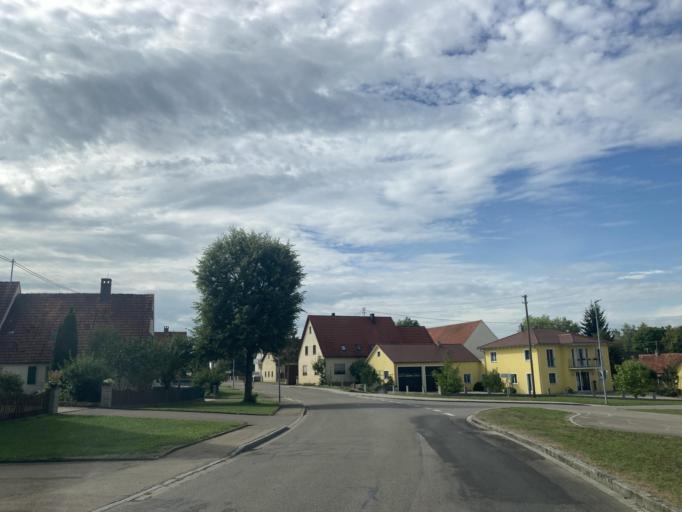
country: DE
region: Bavaria
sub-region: Swabia
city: Alerheim
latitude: 48.8434
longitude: 10.6236
